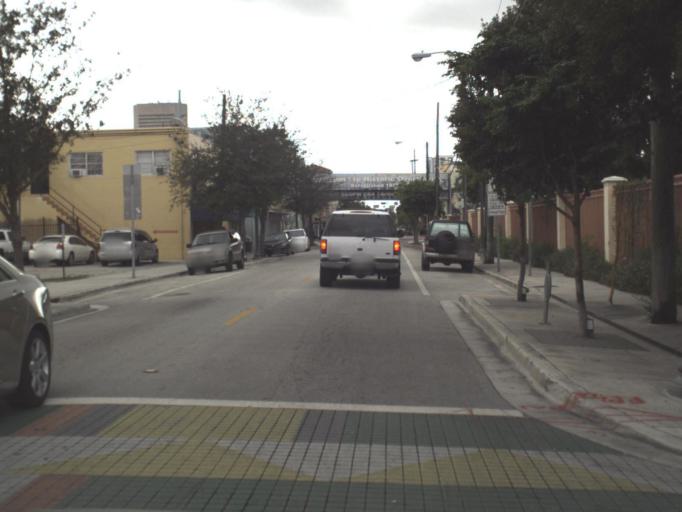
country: US
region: Florida
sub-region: Miami-Dade County
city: Miami
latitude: 25.7859
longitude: -80.1999
